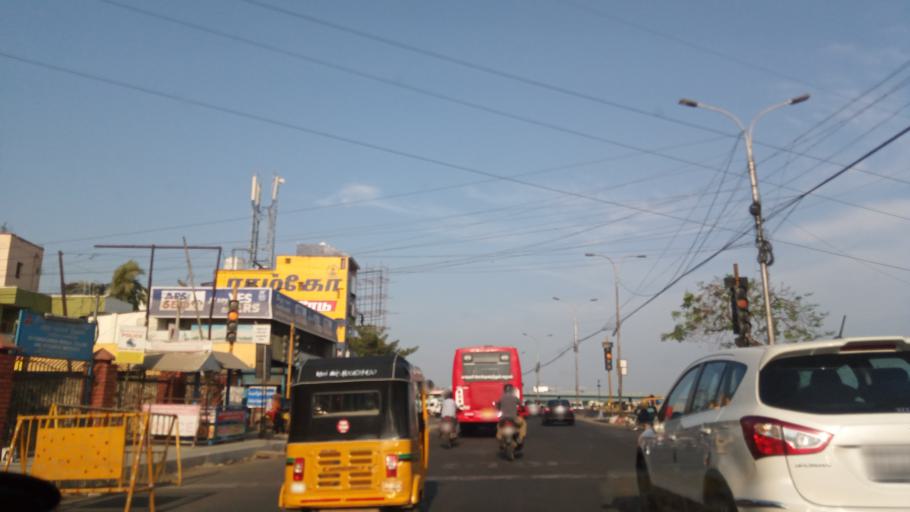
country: IN
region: Tamil Nadu
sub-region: Thiruvallur
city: Porur
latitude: 13.0363
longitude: 80.1462
